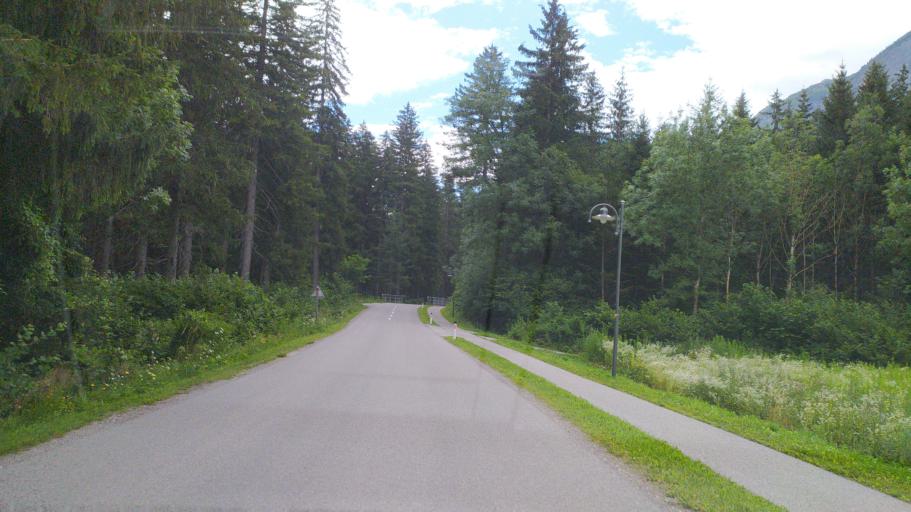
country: AT
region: Tyrol
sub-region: Politischer Bezirk Lienz
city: Lavant
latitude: 46.7961
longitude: 12.8498
